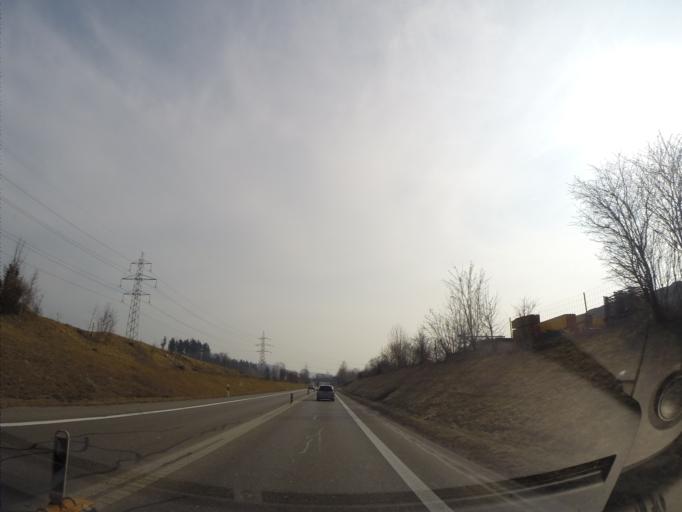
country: CH
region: Zurich
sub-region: Bezirk Winterthur
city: Hettlingen
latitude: 47.5388
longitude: 8.6918
